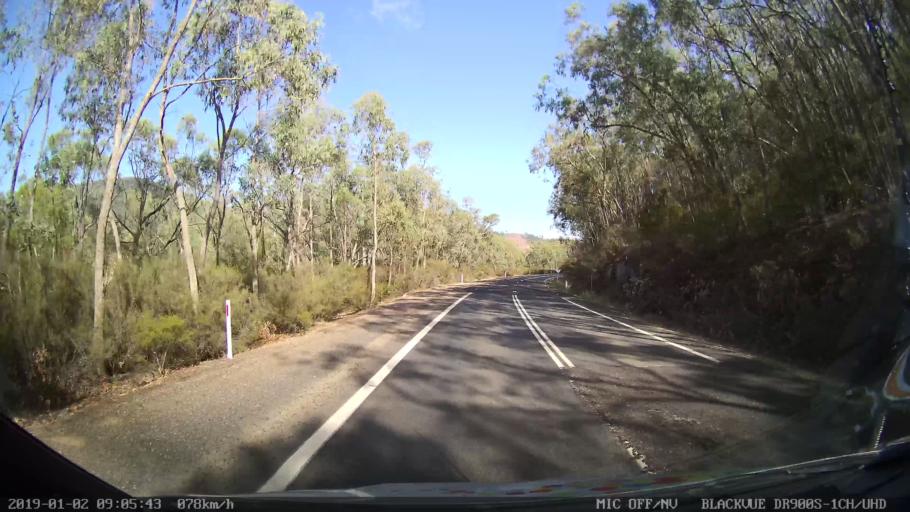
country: AU
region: New South Wales
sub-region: Tumut Shire
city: Tumut
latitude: -35.5592
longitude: 148.3055
